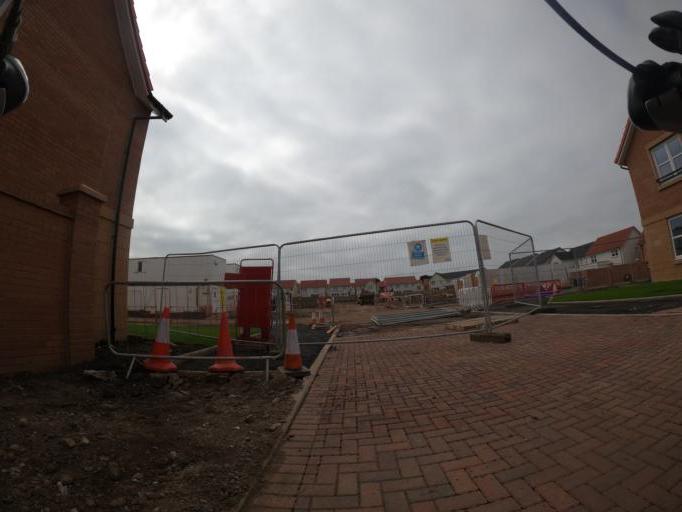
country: GB
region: Scotland
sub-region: East Lothian
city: Musselburgh
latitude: 55.9341
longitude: -3.0842
